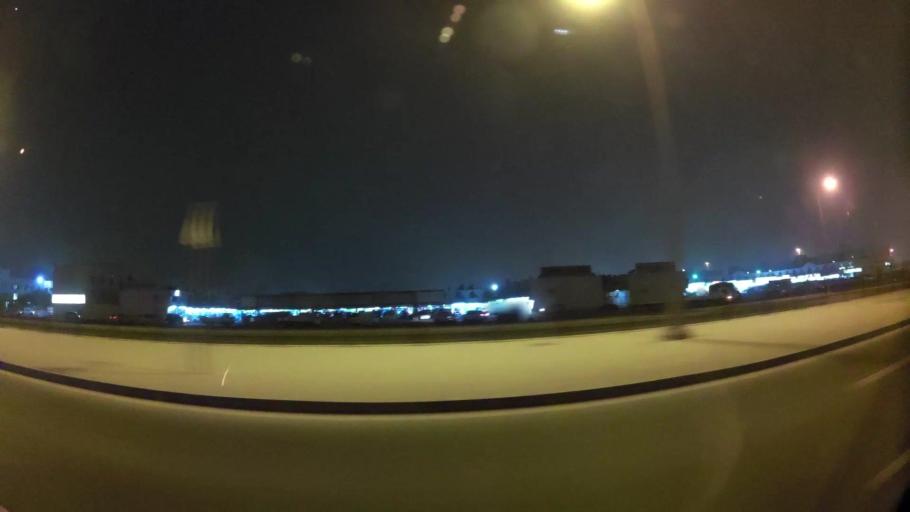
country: QA
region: Baladiyat ad Dawhah
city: Doha
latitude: 25.2471
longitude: 51.4734
